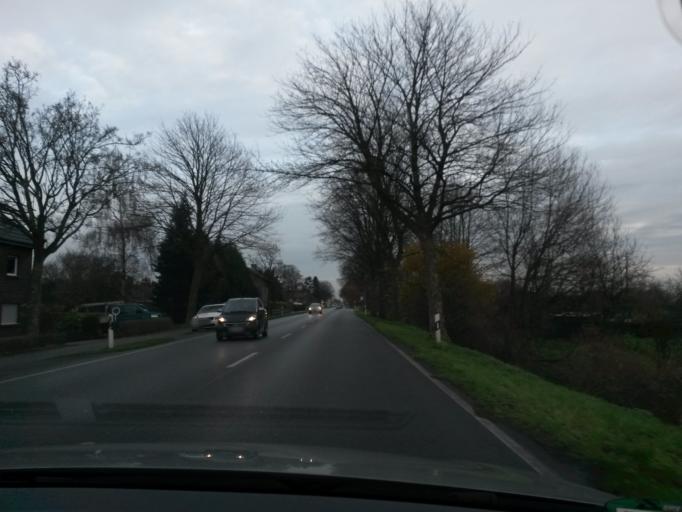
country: DE
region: North Rhine-Westphalia
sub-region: Regierungsbezirk Dusseldorf
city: Wesel
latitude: 51.6235
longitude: 6.5739
